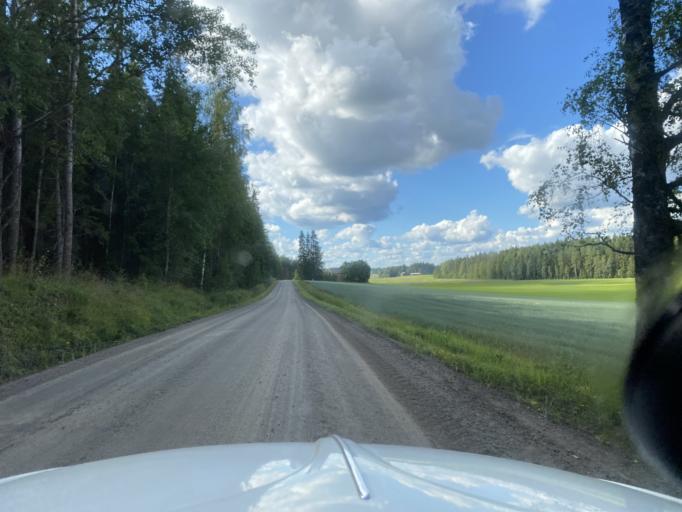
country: FI
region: Pirkanmaa
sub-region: Lounais-Pirkanmaa
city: Punkalaidun
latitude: 61.1223
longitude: 23.2651
